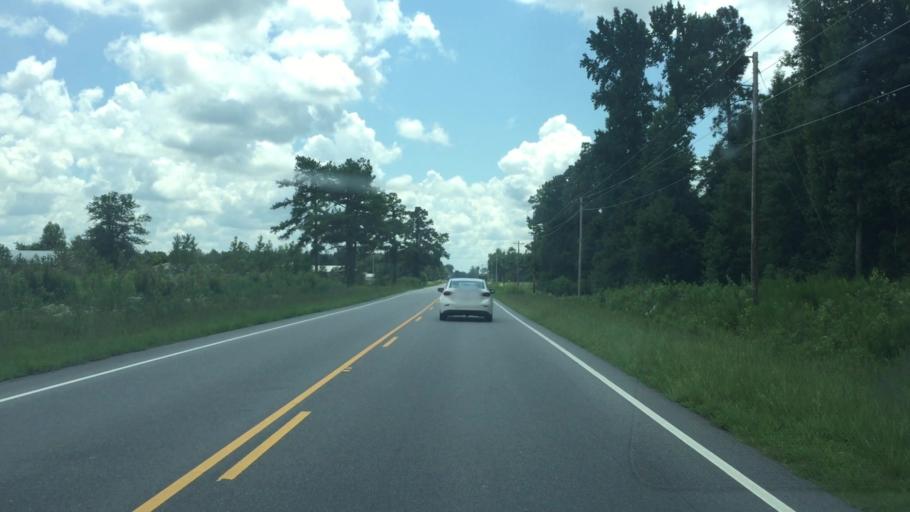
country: US
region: North Carolina
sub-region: Columbus County
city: Chadbourn
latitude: 34.2311
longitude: -78.8244
